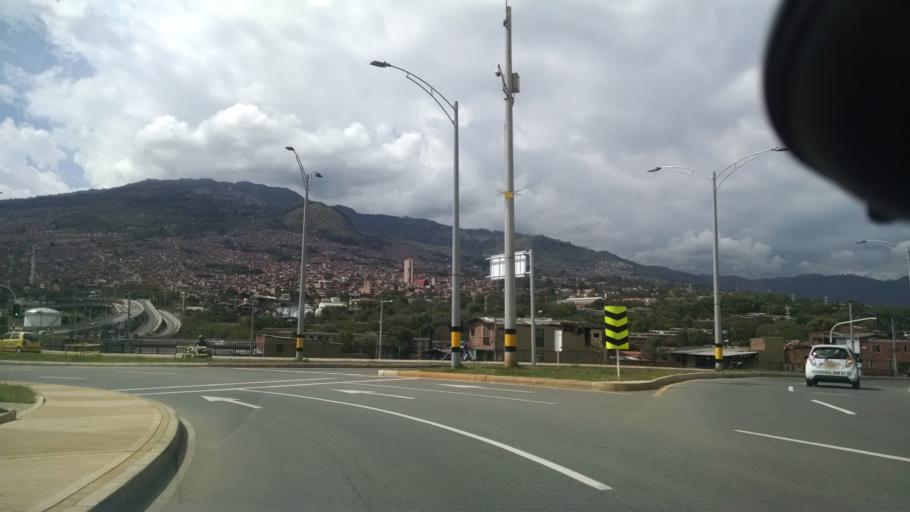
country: CO
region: Antioquia
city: Medellin
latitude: 6.2859
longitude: -75.5643
